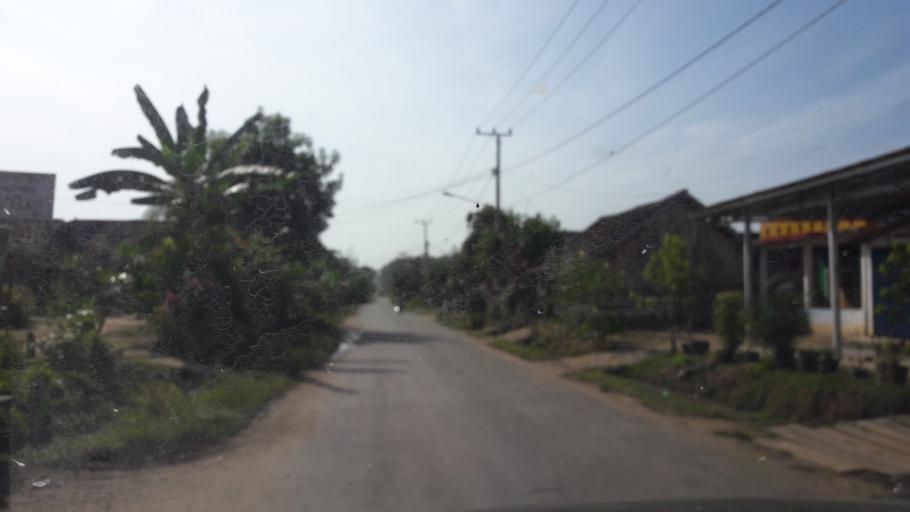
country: ID
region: South Sumatra
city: Gunungmenang
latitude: -3.3124
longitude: 103.9781
